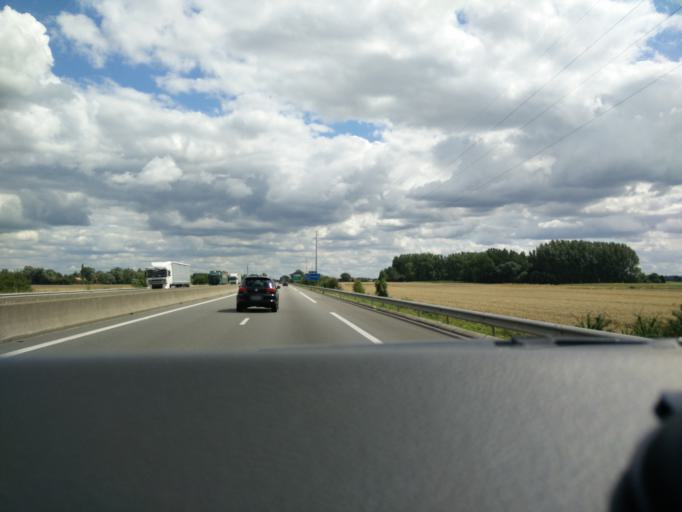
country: FR
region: Nord-Pas-de-Calais
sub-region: Departement du Nord
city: Herzeele
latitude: 50.8772
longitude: 2.5231
